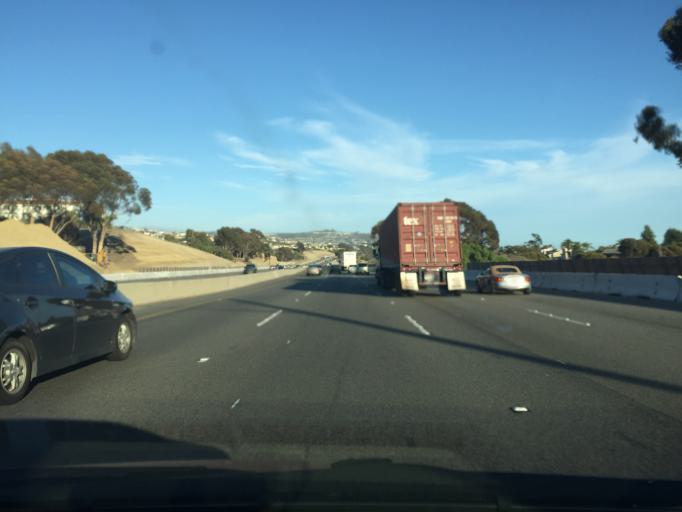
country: US
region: California
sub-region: Orange County
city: San Juan Capistrano
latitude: 33.4565
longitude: -117.6523
